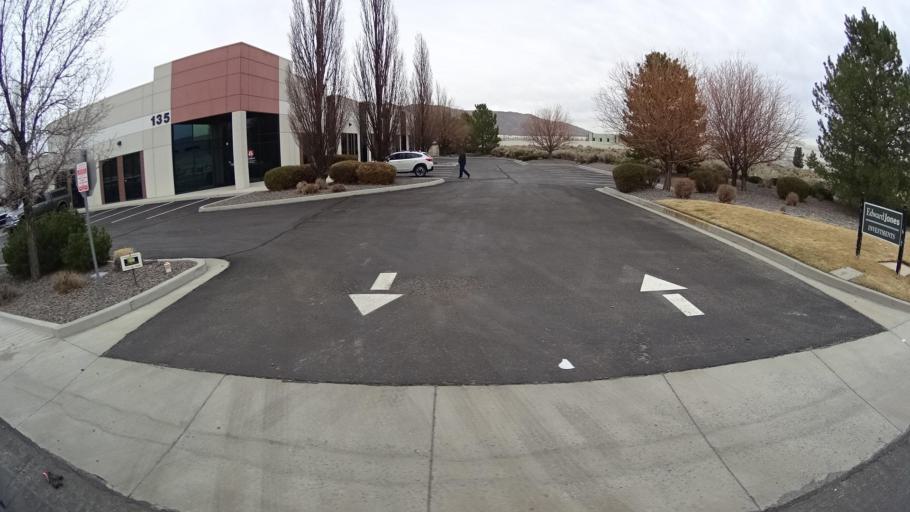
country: US
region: Nevada
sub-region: Washoe County
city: Spanish Springs
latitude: 39.6693
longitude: -119.7057
